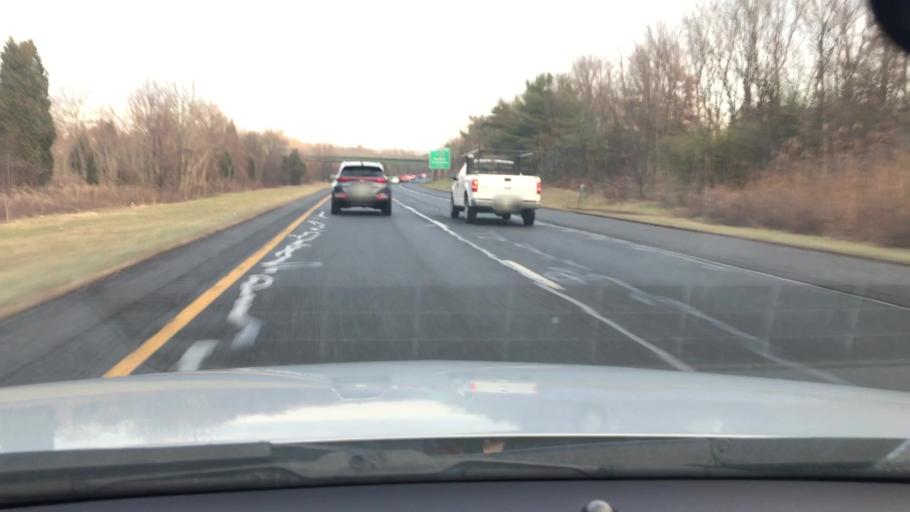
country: US
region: New Jersey
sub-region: Camden County
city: Blackwood
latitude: 39.8108
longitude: -75.1054
